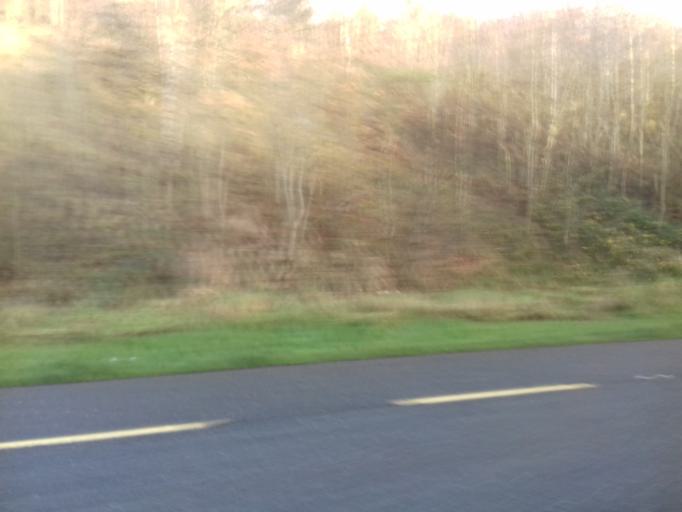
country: IE
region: Ulster
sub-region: County Monaghan
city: Carrickmacross
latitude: 53.9766
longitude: -6.7036
